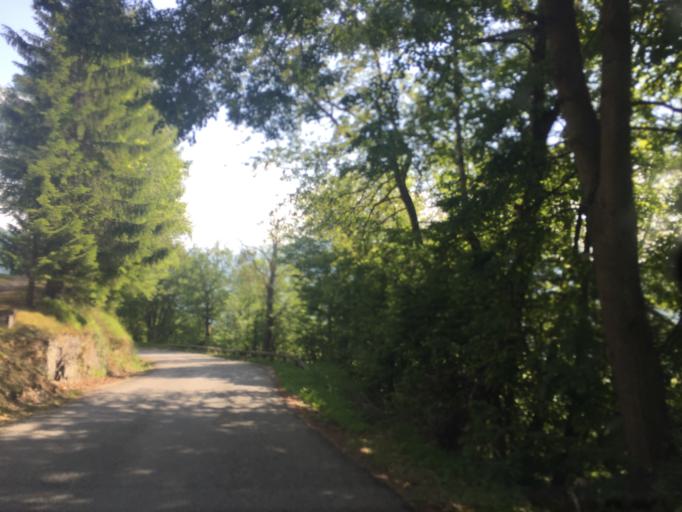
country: FR
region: Rhone-Alpes
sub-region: Departement de la Savoie
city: Aiton
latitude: 45.5220
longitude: 6.3274
